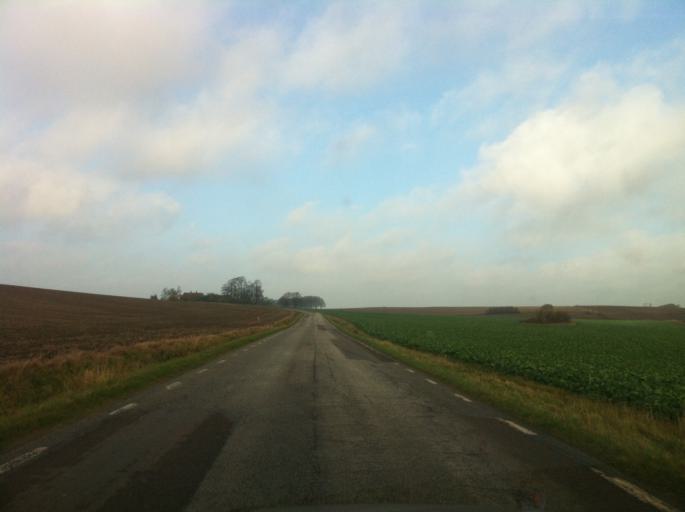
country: SE
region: Skane
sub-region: Landskrona
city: Asmundtorp
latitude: 55.9273
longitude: 12.8894
